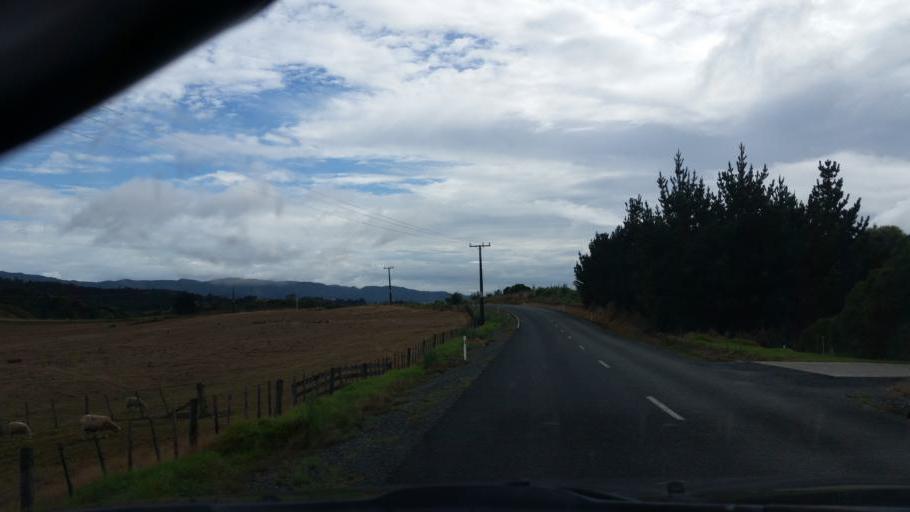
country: NZ
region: Auckland
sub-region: Auckland
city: Wellsford
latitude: -36.1495
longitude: 174.5443
